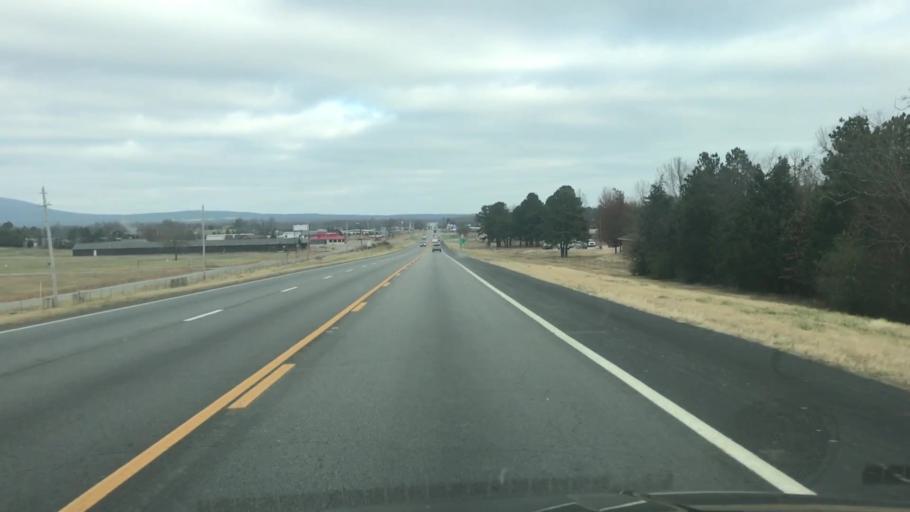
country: US
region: Arkansas
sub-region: Scott County
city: Waldron
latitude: 34.8923
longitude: -94.1076
